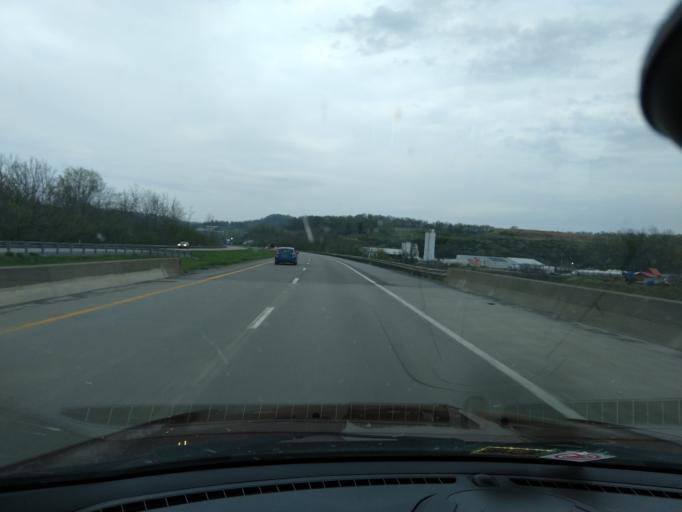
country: US
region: West Virginia
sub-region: Lewis County
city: Weston
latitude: 39.0916
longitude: -80.3934
